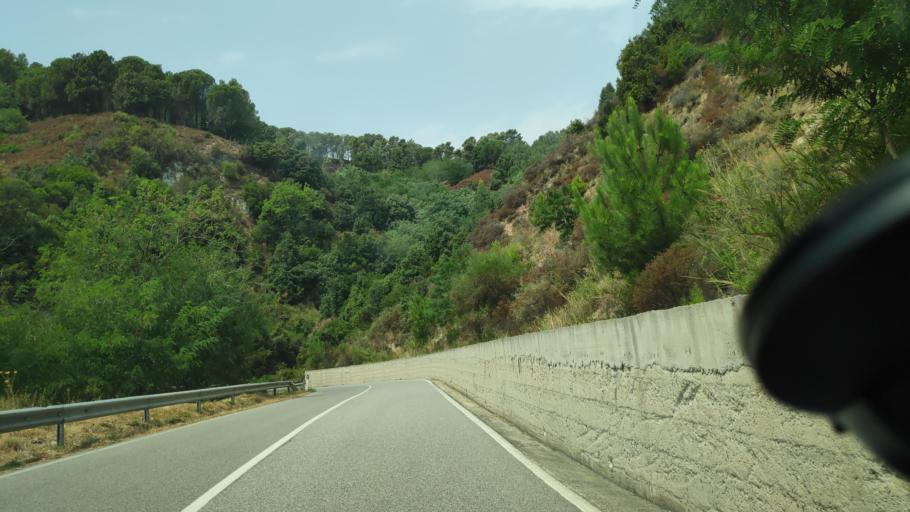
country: IT
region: Calabria
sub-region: Provincia di Catanzaro
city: San Sostene
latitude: 38.6402
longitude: 16.5088
